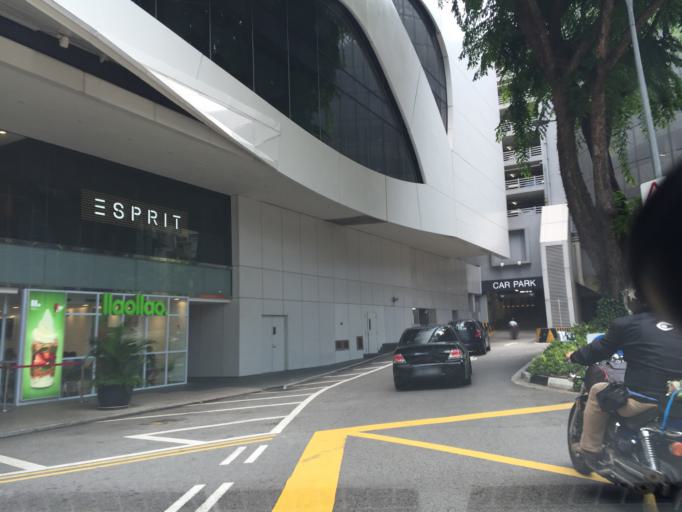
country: SG
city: Singapore
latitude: 1.3004
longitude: 103.8453
